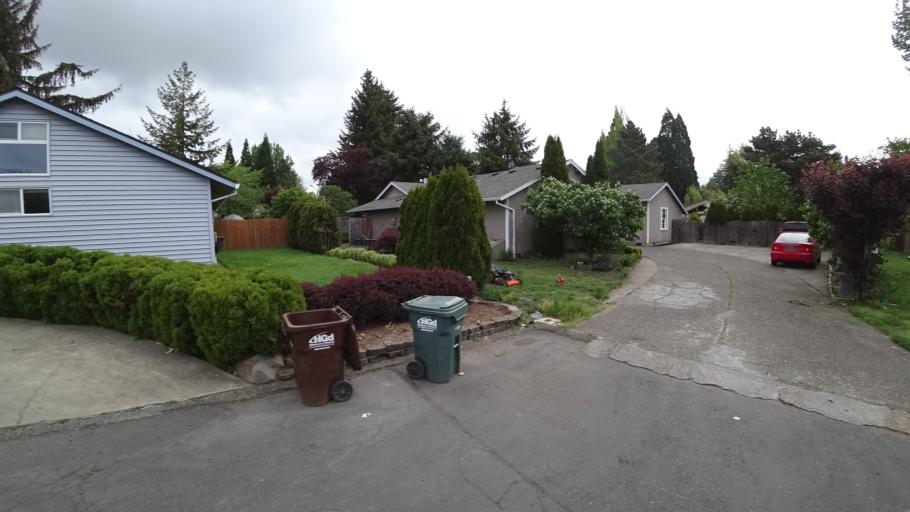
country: US
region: Oregon
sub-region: Washington County
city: Hillsboro
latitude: 45.5351
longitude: -122.9640
